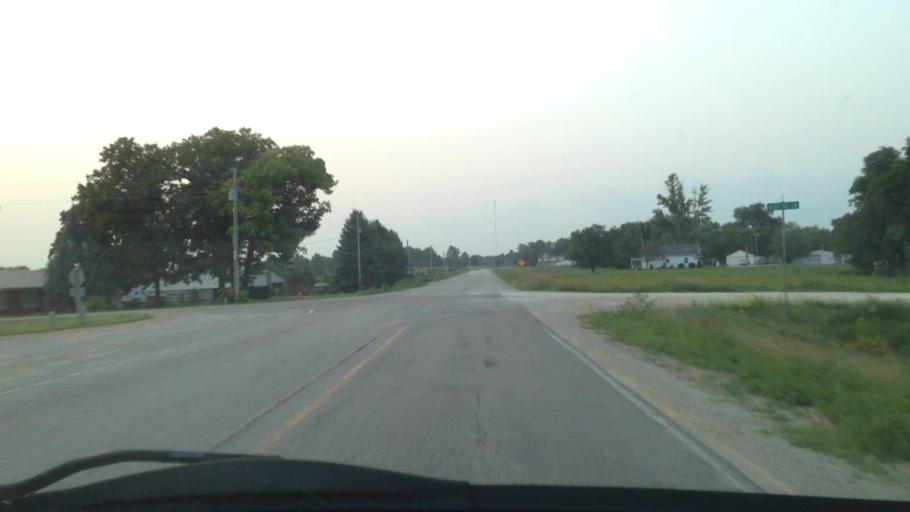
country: US
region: Iowa
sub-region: Benton County
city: Urbana
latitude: 42.1382
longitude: -91.8765
